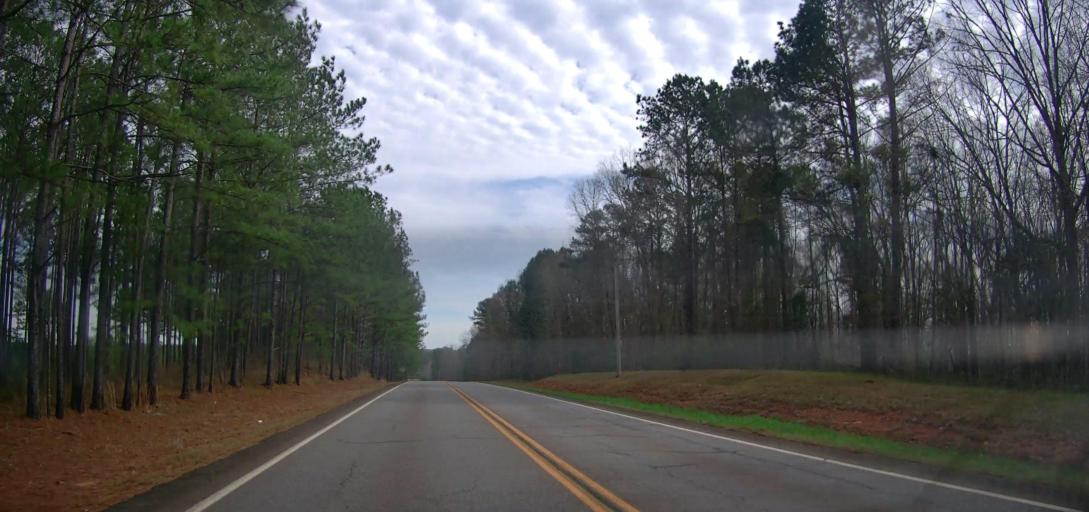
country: US
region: Georgia
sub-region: Jones County
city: Gray
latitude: 33.0047
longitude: -83.7010
